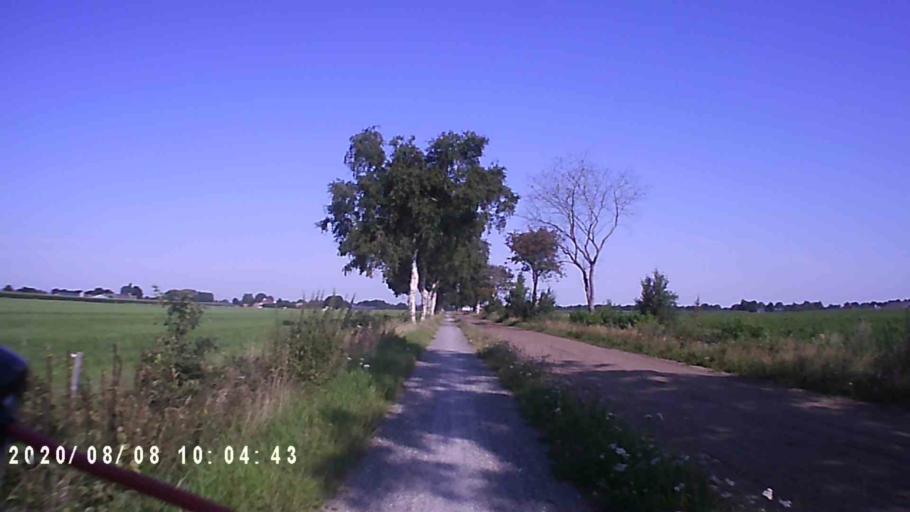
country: NL
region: Groningen
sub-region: Gemeente Leek
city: Leek
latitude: 53.1120
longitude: 6.3755
